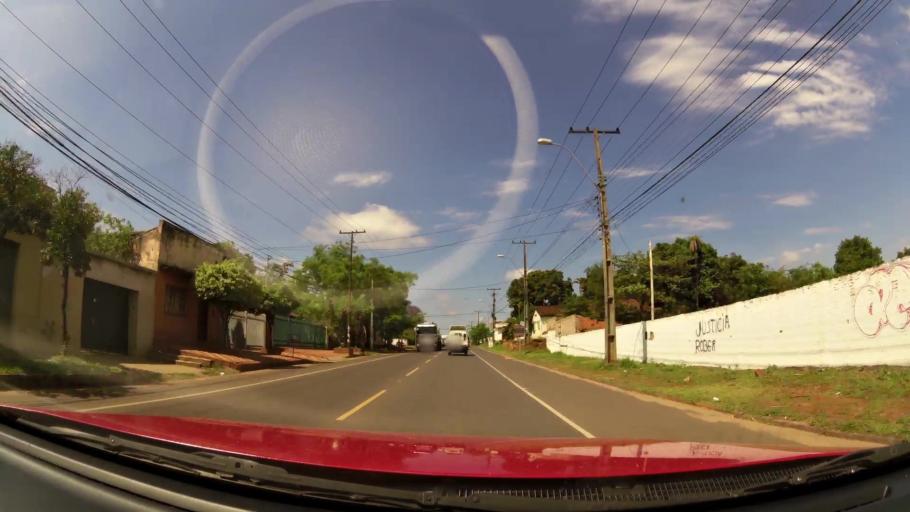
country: PY
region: Central
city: San Lorenzo
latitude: -25.2757
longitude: -57.4968
